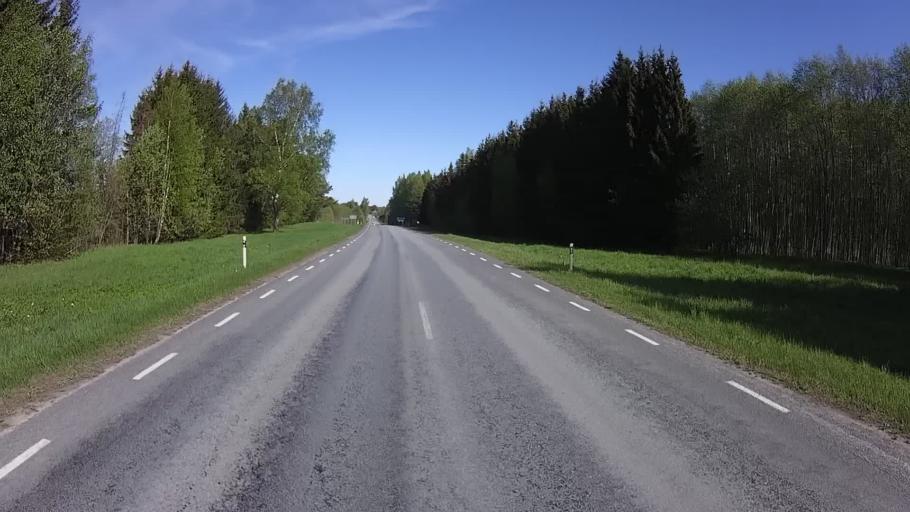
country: EE
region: Polvamaa
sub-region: Polva linn
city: Polva
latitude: 58.2333
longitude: 27.0206
